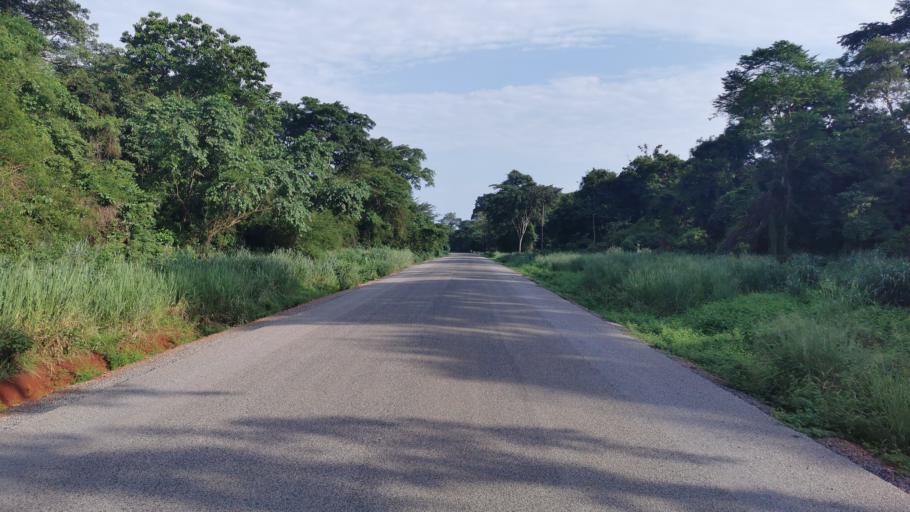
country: ET
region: Gambela
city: Gambela
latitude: 7.7167
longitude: 34.6615
